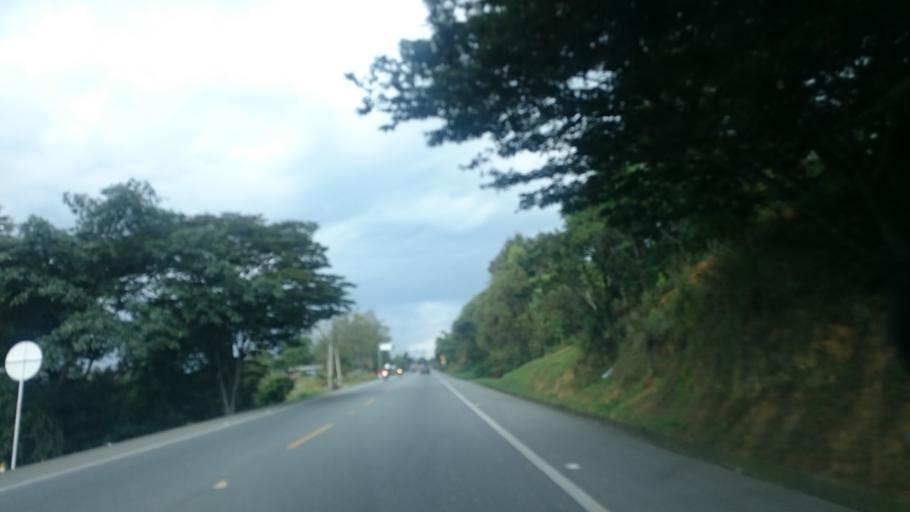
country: CO
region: Cauca
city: Cajibio
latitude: 2.6033
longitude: -76.5271
